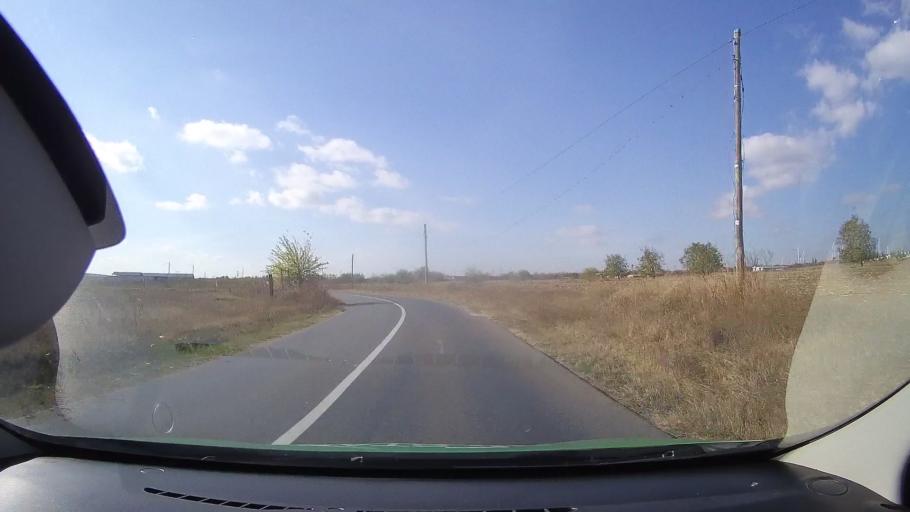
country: RO
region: Constanta
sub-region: Comuna Cogealac
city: Cogealac
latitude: 44.5611
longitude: 28.5770
